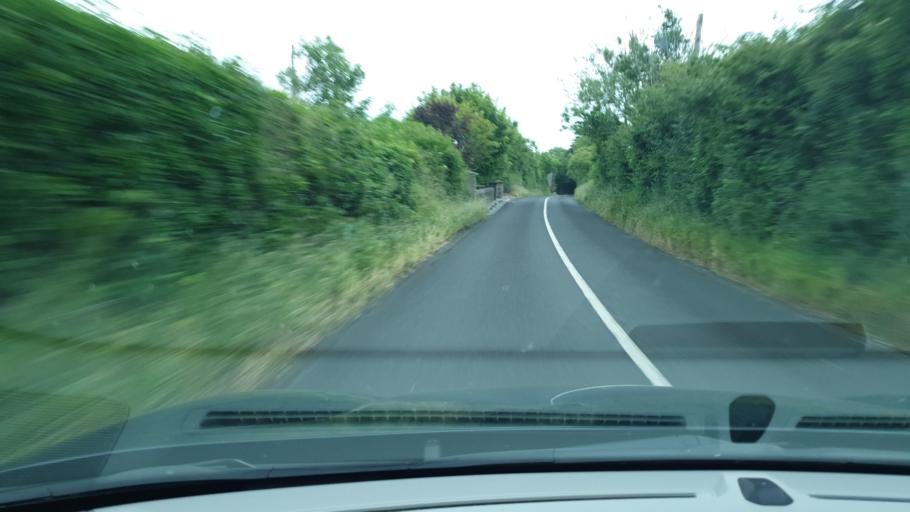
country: IE
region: Leinster
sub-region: An Mhi
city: Navan
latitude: 53.6458
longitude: -6.7161
